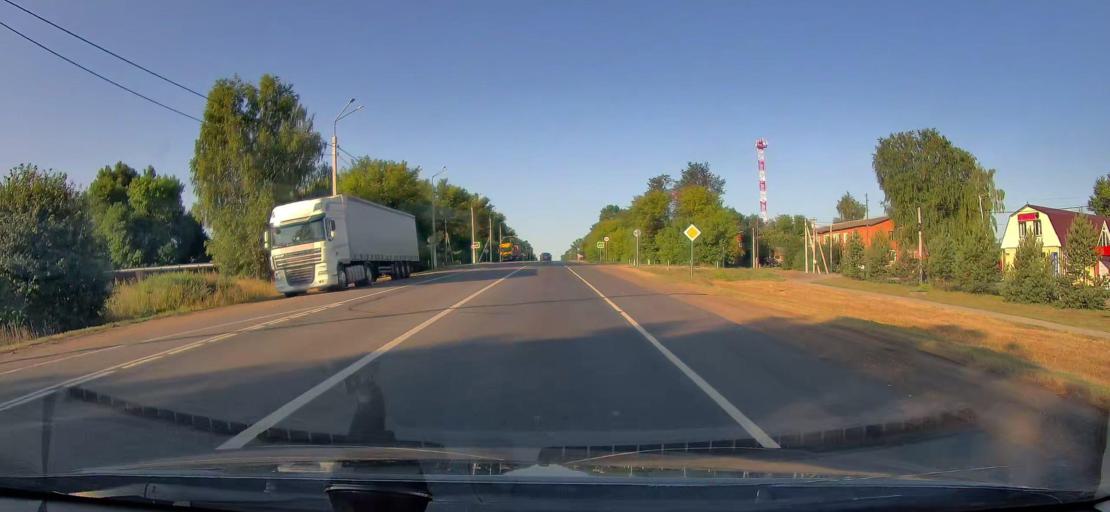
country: RU
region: Tula
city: Plavsk
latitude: 53.6954
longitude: 37.2791
